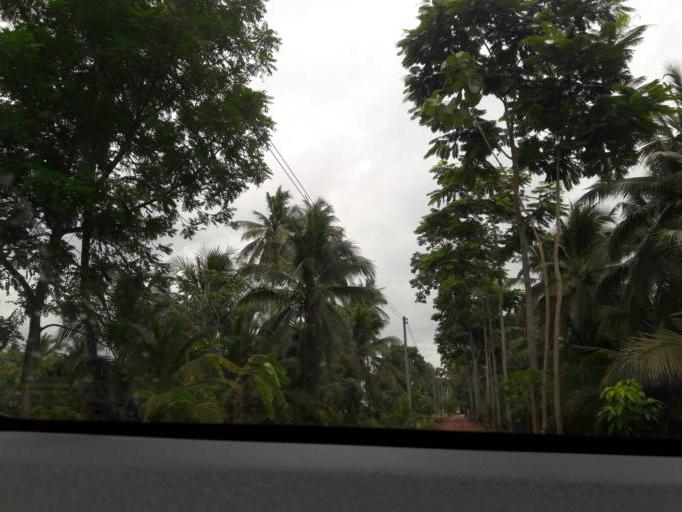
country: TH
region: Ratchaburi
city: Damnoen Saduak
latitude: 13.5733
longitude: 99.9886
